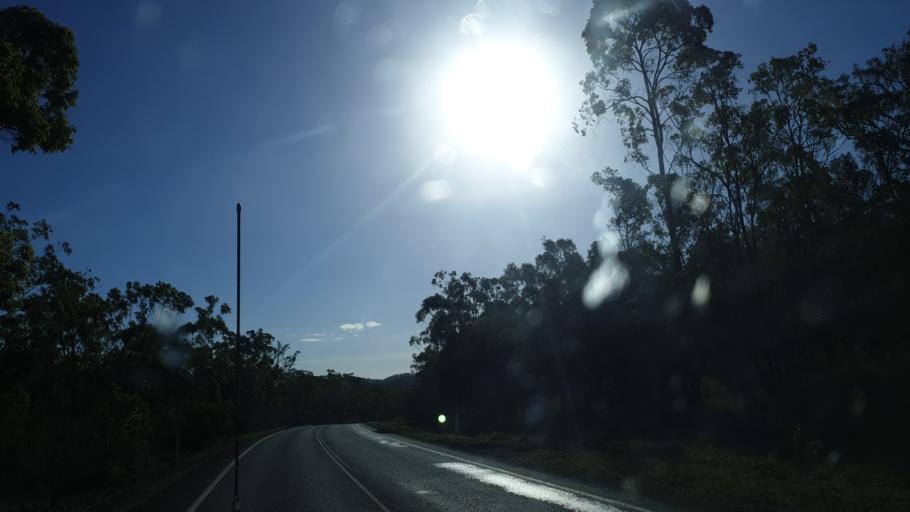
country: AU
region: Queensland
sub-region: Tablelands
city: Atherton
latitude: -17.3623
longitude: 145.4049
